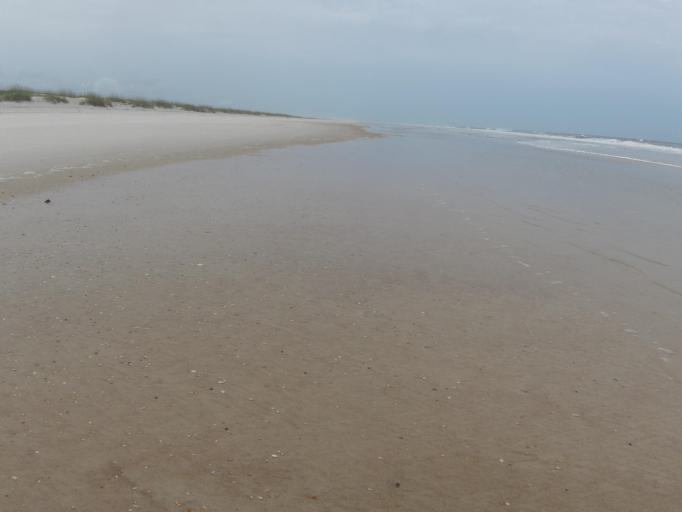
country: US
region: Florida
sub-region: Saint Johns County
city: Saint Augustine
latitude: 29.8944
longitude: -81.2756
